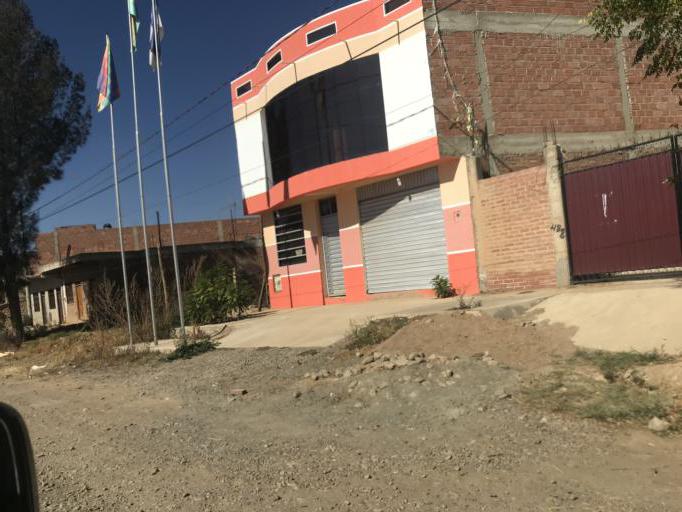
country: BO
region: Cochabamba
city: Cliza
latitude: -17.5838
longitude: -65.9161
